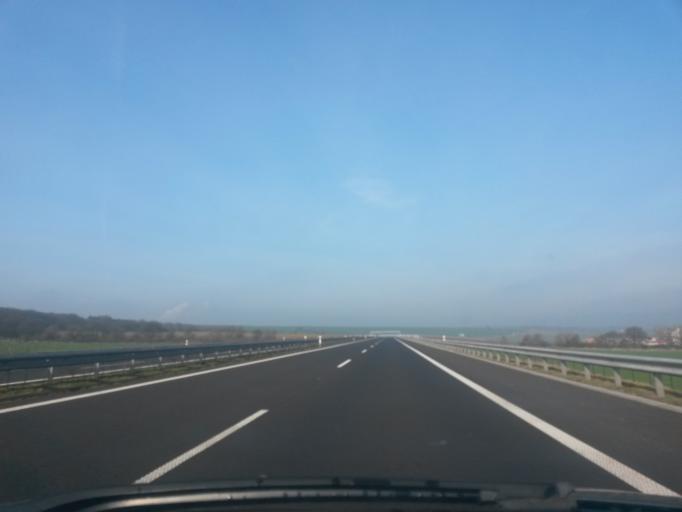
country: CZ
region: Ustecky
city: Udlice
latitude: 50.4144
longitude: 13.4706
